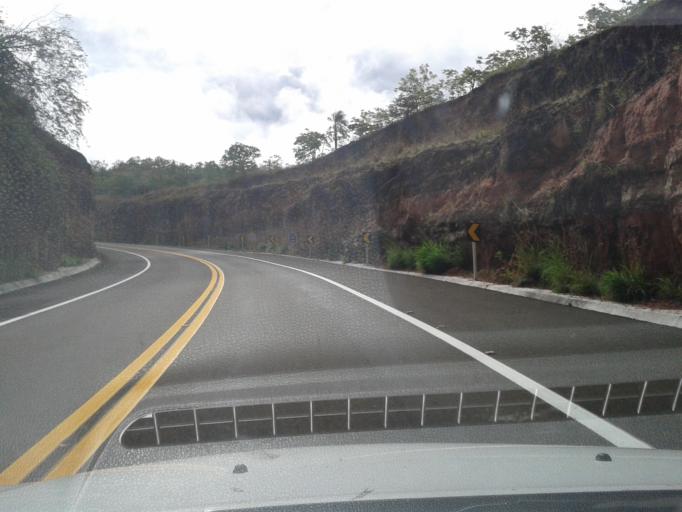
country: BR
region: Minas Gerais
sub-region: Campina Verde
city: Campina Verde
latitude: -19.4070
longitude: -49.5986
